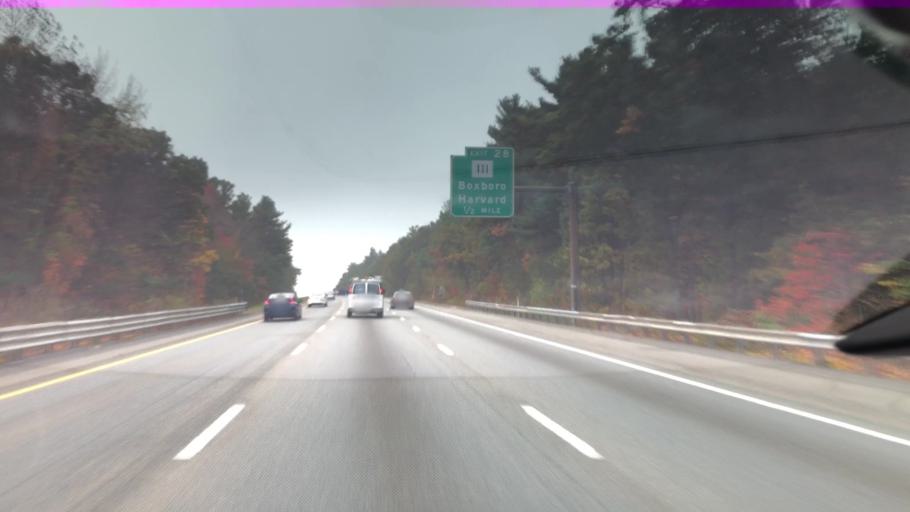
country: US
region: Massachusetts
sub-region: Worcester County
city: Harvard
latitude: 42.4936
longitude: -71.5403
